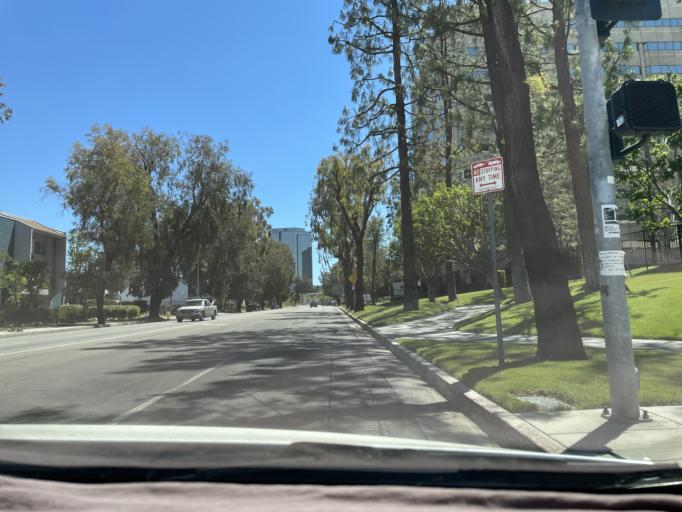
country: US
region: California
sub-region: Los Angeles County
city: Canoga Park
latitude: 34.1855
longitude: -118.6016
